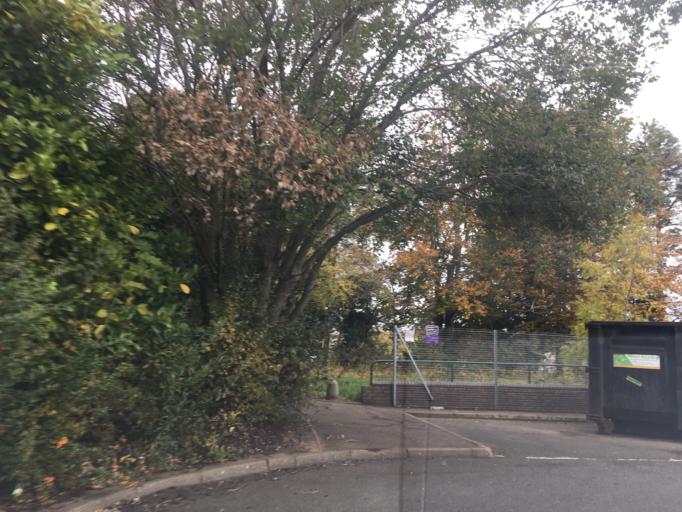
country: GB
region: Scotland
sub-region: Edinburgh
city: Colinton
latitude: 55.9017
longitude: -3.2255
